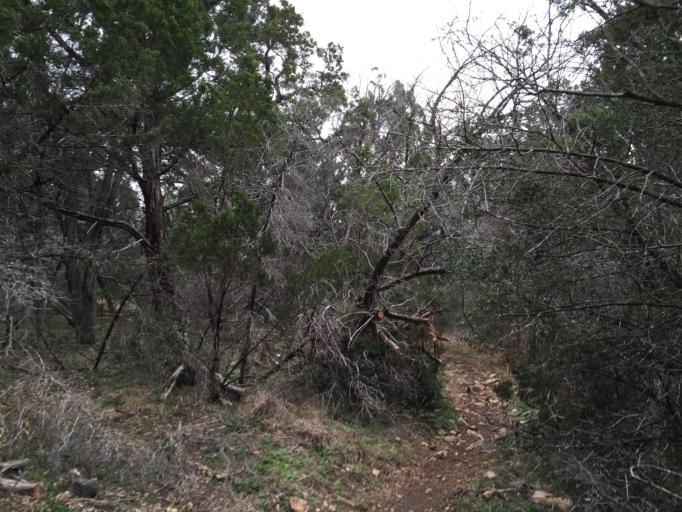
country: US
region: Texas
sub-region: Travis County
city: Rollingwood
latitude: 30.2473
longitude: -97.8209
